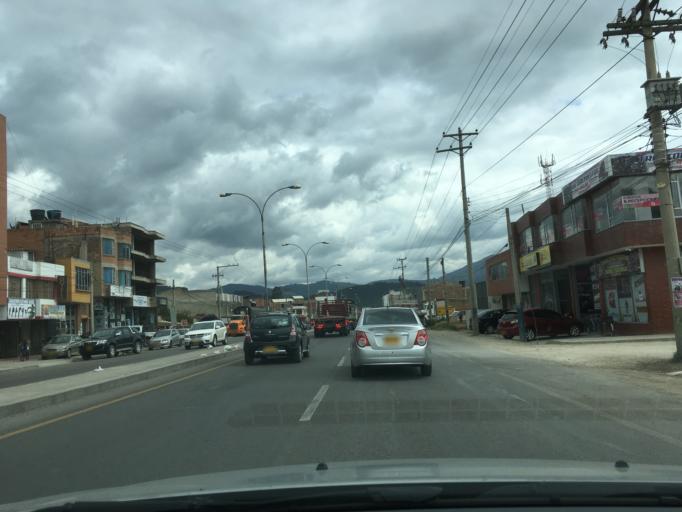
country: CO
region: Boyaca
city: Duitama
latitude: 5.8077
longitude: -73.0249
